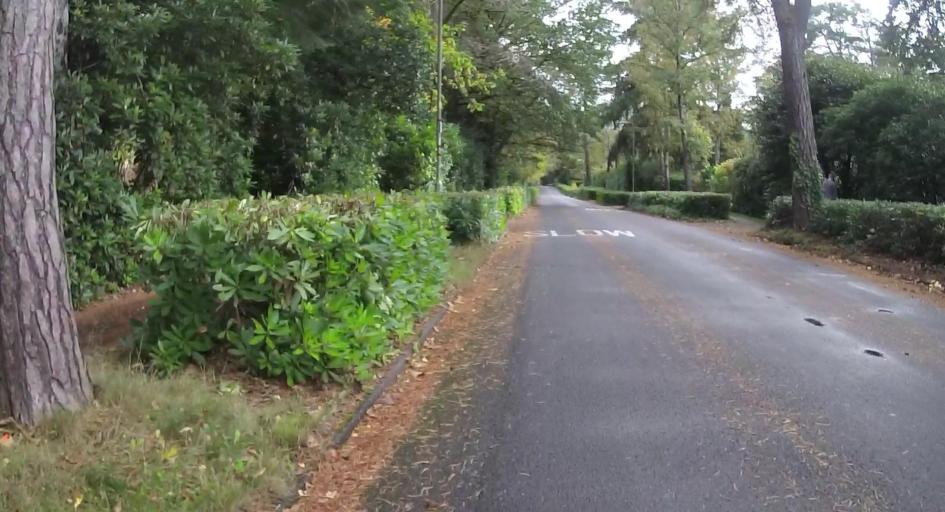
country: GB
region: England
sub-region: Hampshire
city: Fleet
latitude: 51.2817
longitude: -0.8565
